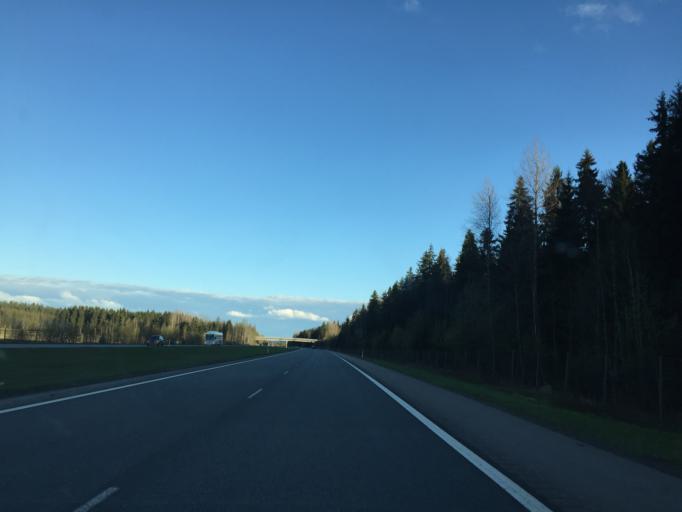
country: FI
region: Haeme
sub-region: Haemeenlinna
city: Tervakoski
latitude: 60.7988
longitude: 24.6864
